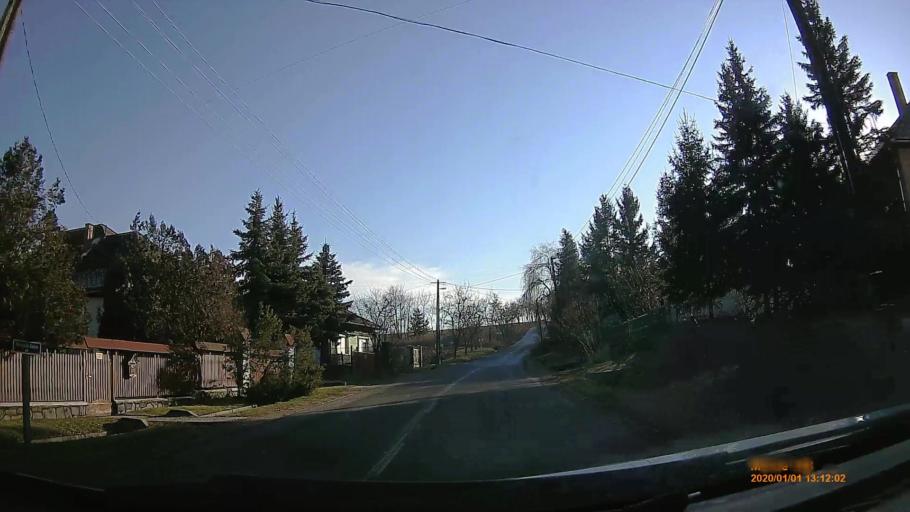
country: HU
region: Heves
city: Parad
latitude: 47.9351
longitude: 20.0245
